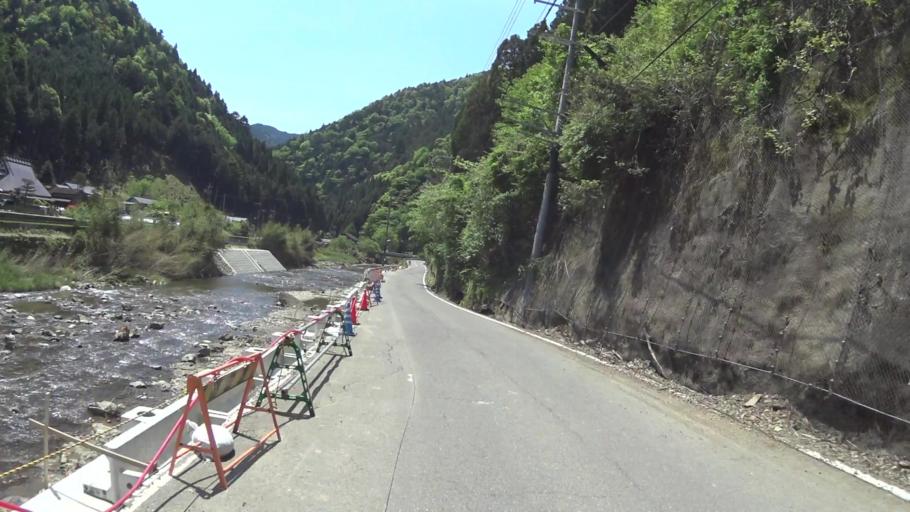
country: JP
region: Shiga Prefecture
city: Kitahama
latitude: 35.2071
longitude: 135.7488
